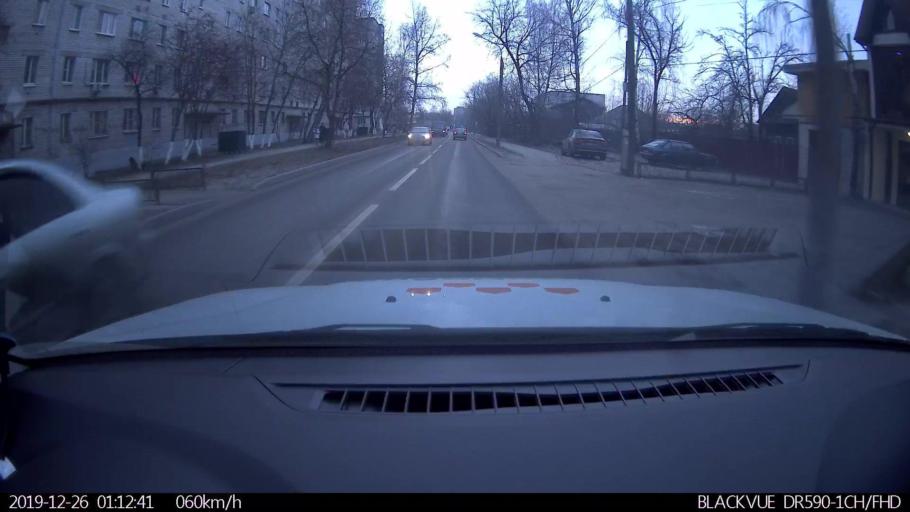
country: RU
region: Nizjnij Novgorod
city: Nizhniy Novgorod
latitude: 56.2827
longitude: 43.9147
